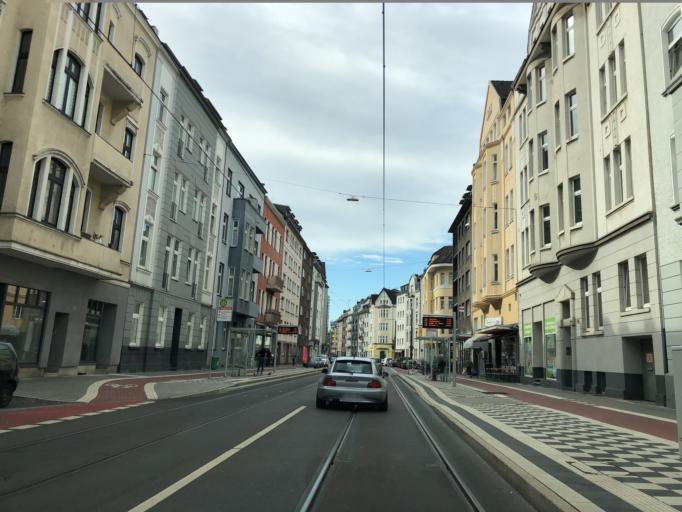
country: DE
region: North Rhine-Westphalia
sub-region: Regierungsbezirk Dusseldorf
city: Dusseldorf
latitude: 51.2121
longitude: 6.7591
